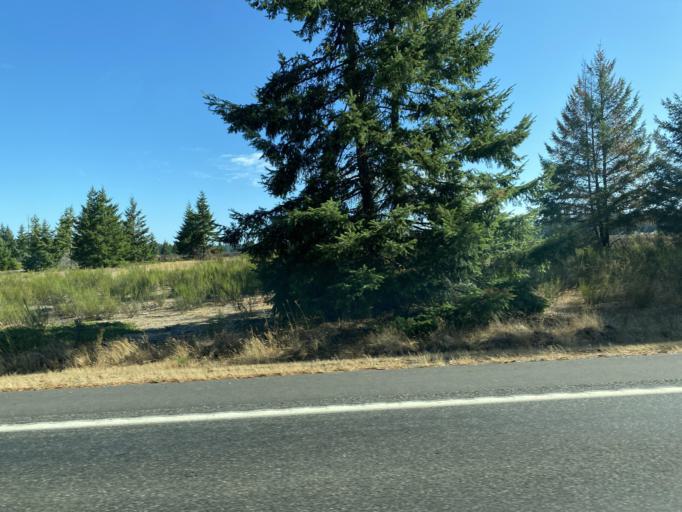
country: US
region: Washington
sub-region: Thurston County
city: Rainier
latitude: 46.9051
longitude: -122.7277
